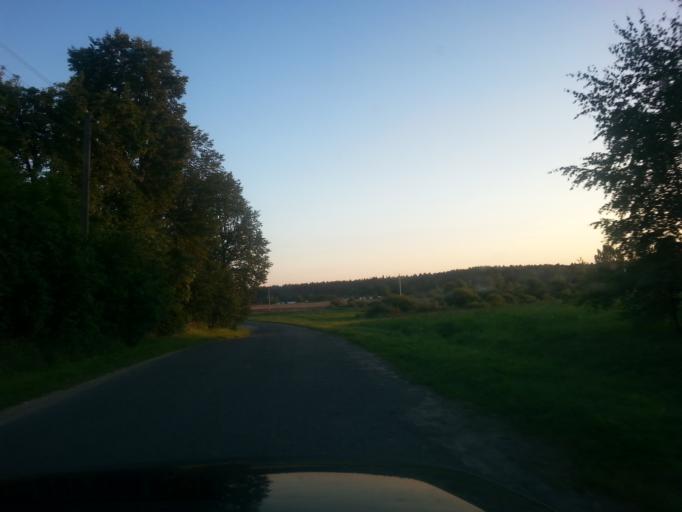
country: BY
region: Minsk
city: Narach
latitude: 54.9704
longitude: 26.6373
